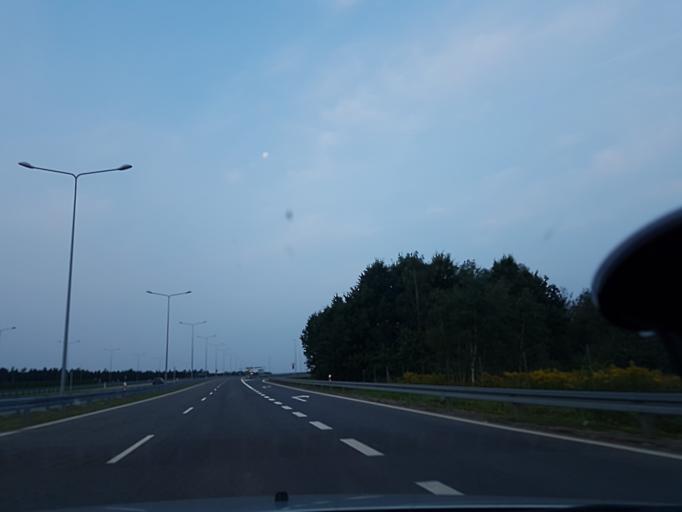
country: PL
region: Lodz Voivodeship
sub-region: Powiat lodzki wschodni
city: Rzgow
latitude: 51.6402
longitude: 19.5043
